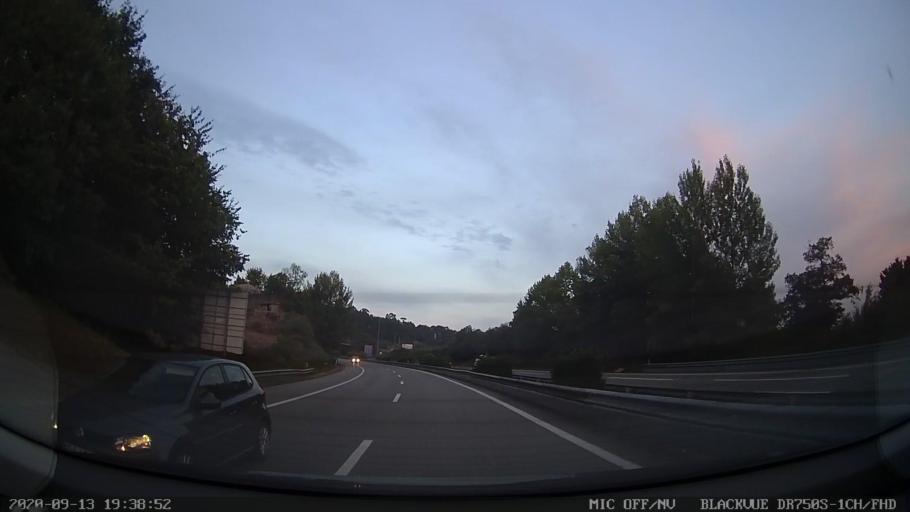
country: PT
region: Porto
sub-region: Marco de Canaveses
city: Marco de Canavezes
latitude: 41.2184
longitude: -8.1524
